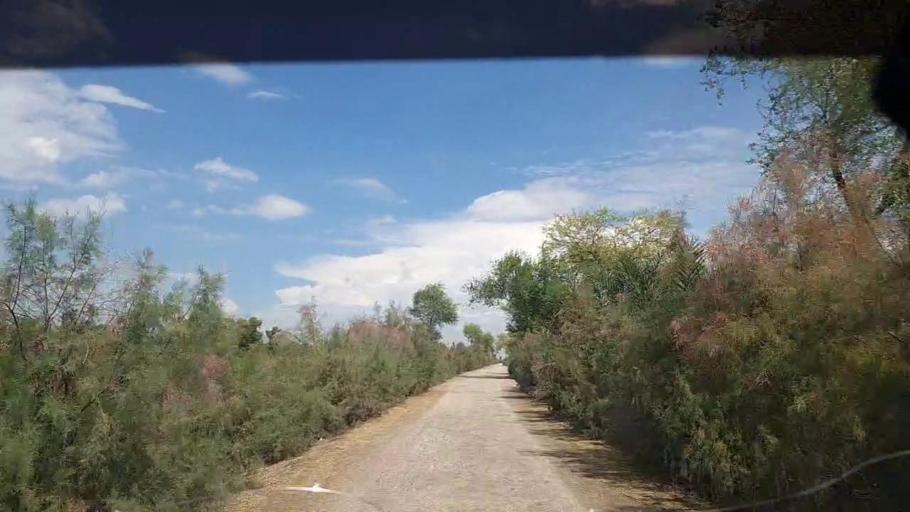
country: PK
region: Sindh
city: Ghauspur
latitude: 28.1490
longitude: 68.9940
